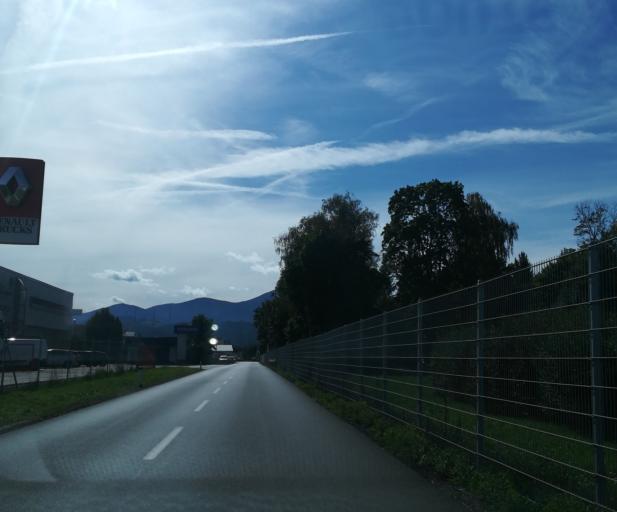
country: AT
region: Styria
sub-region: Politischer Bezirk Murtal
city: Zeltweg
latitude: 47.1988
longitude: 14.7640
